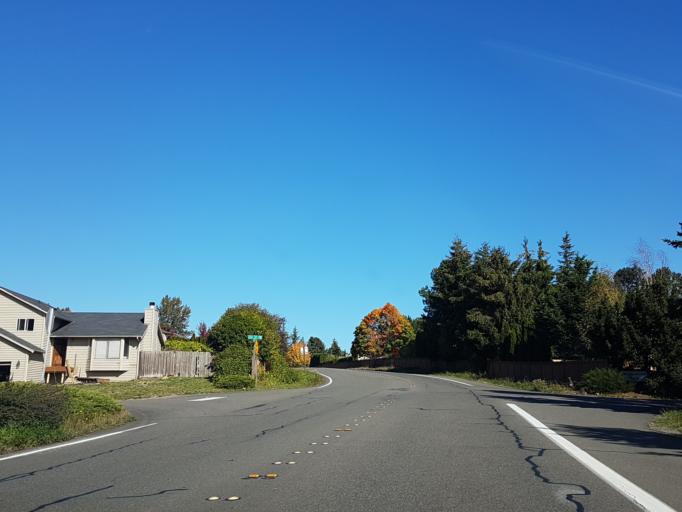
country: US
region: Washington
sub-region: Snohomish County
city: Brier
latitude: 47.7857
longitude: -122.2522
